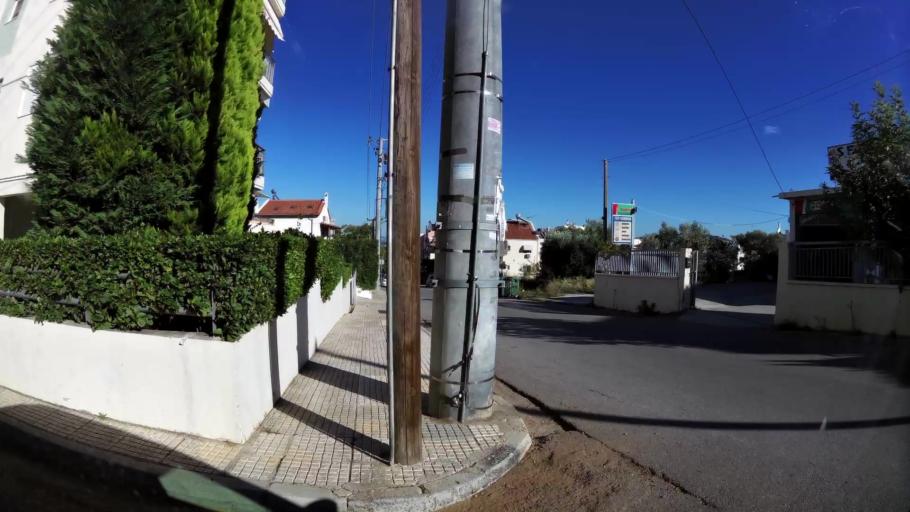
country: GR
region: Attica
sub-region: Nomarchia Anatolikis Attikis
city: Leondarion
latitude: 37.9796
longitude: 23.8475
